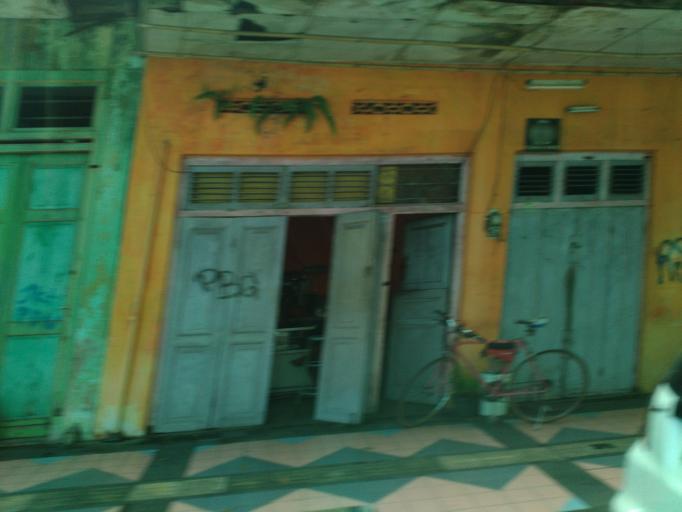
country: ID
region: Central Java
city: Klaten
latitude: -7.7007
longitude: 110.6046
